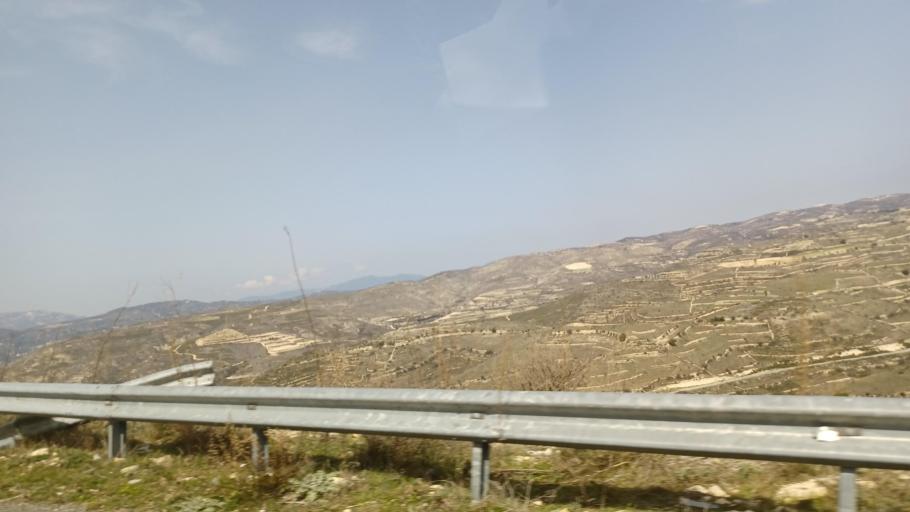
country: CY
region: Limassol
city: Pachna
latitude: 34.8047
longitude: 32.7555
